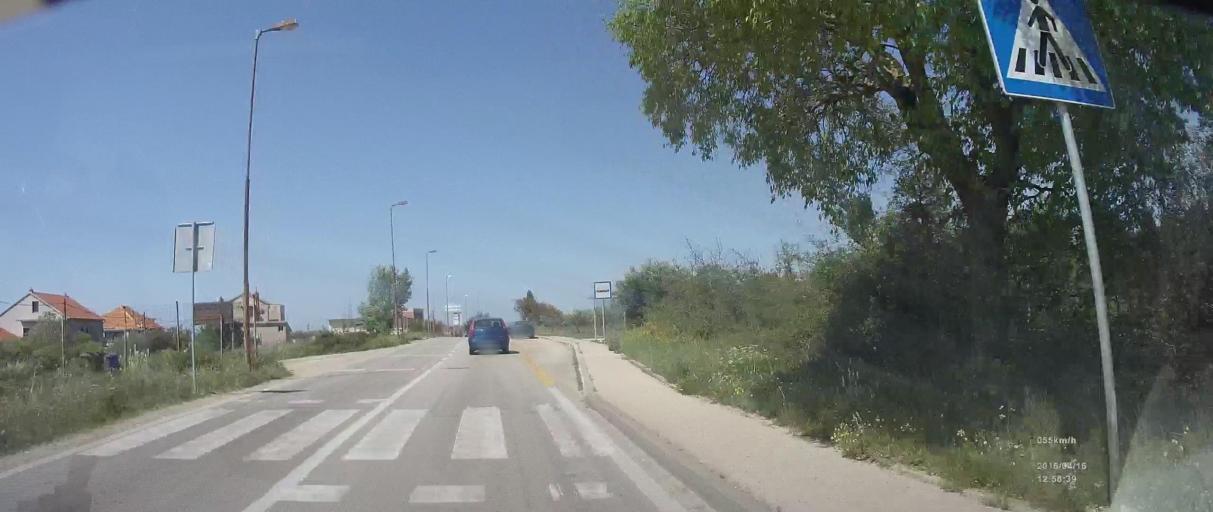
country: HR
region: Sibensko-Kniniska
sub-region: Grad Sibenik
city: Sibenik
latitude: 43.7101
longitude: 15.9211
